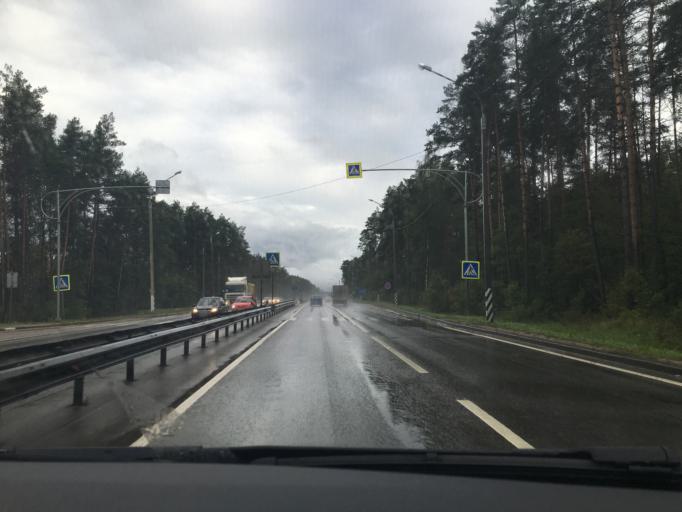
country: RU
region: Kaluga
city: Obninsk
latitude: 55.0617
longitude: 36.6212
